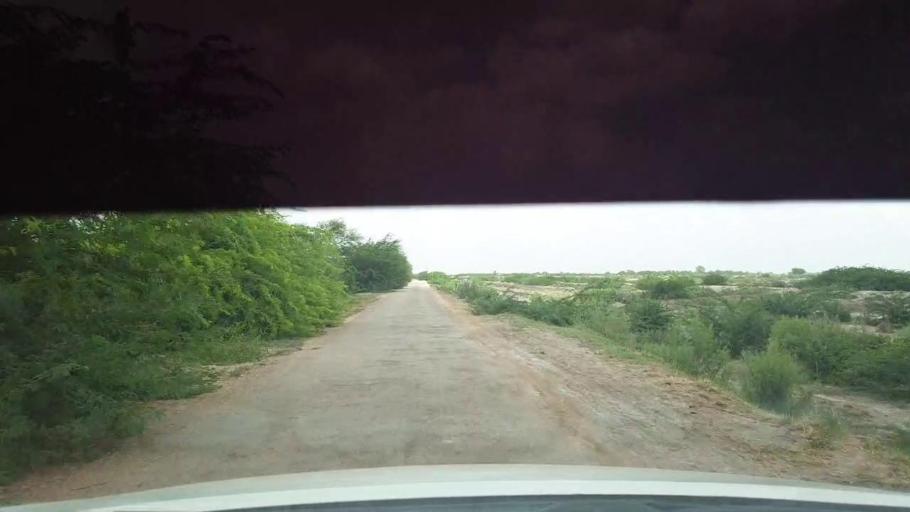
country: PK
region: Sindh
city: Kadhan
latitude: 24.4817
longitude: 69.0663
